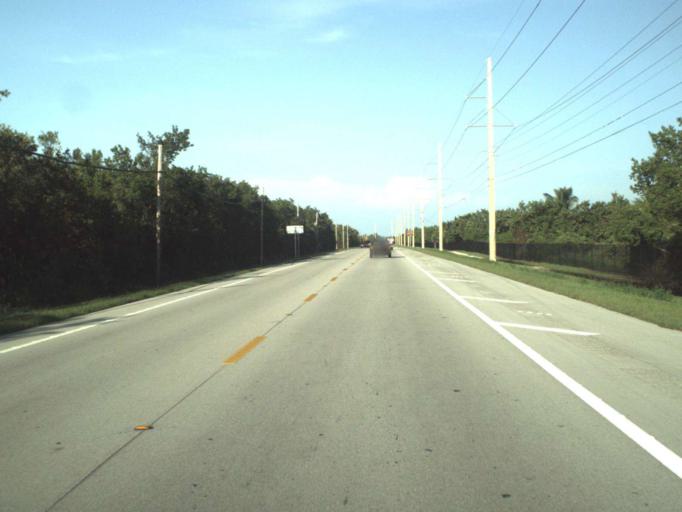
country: US
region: Florida
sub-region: Monroe County
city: Islamorada
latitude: 24.8076
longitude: -80.8378
